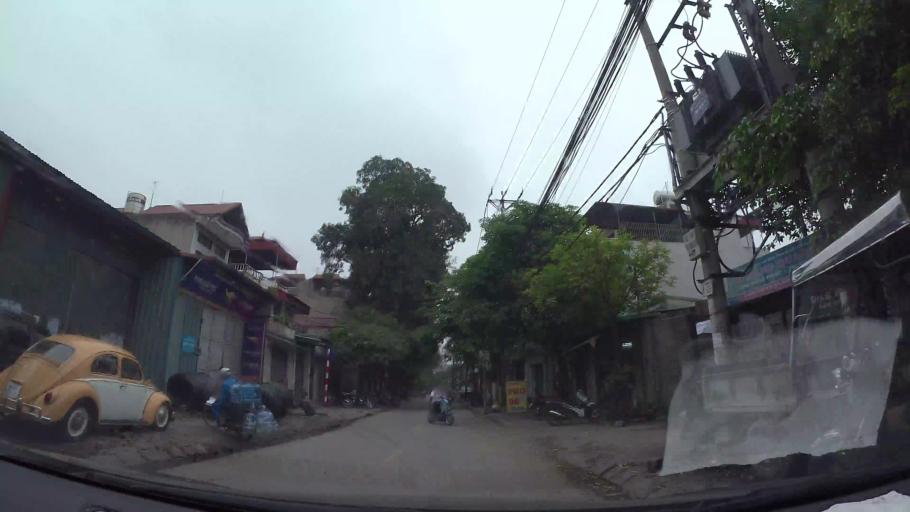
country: VN
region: Hung Yen
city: Van Giang
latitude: 20.9781
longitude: 105.8916
